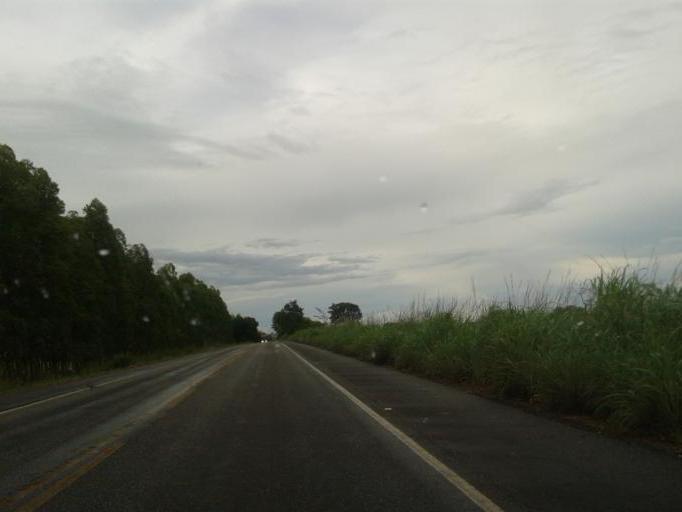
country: BR
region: Goias
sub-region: Mozarlandia
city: Mozarlandia
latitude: -14.8789
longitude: -50.5531
